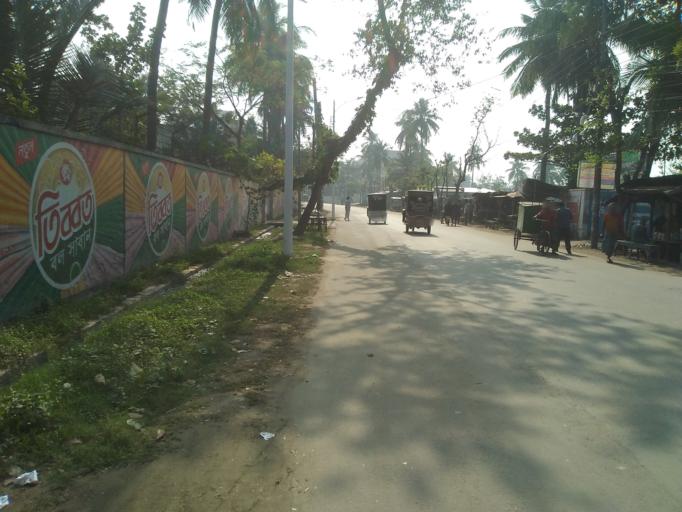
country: BD
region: Khulna
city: Khulna
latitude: 22.8059
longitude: 89.5774
